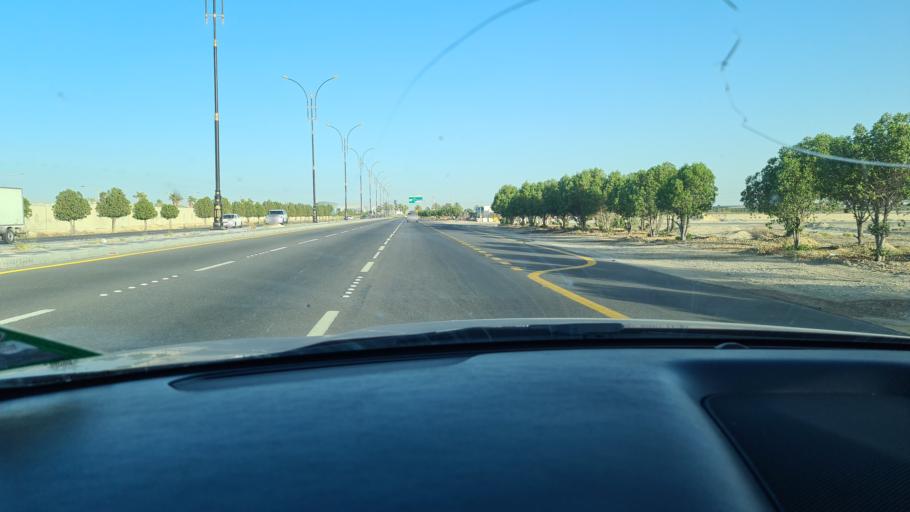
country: SA
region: Eastern Province
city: Al Jubayl
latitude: 26.9314
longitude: 49.7084
